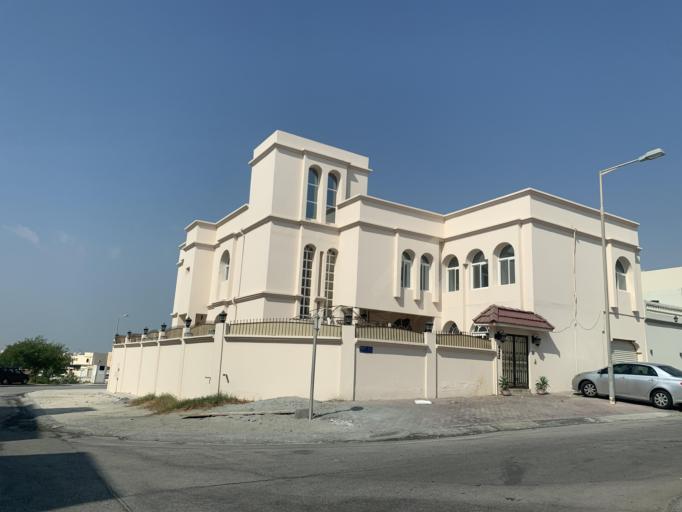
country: BH
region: Central Governorate
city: Madinat Hamad
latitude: 26.1122
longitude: 50.5022
